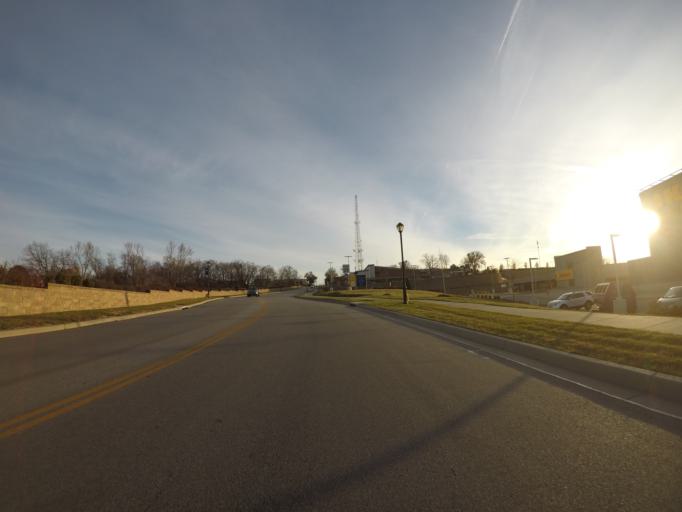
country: US
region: Kansas
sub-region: Johnson County
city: Merriam
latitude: 39.0190
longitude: -94.6898
